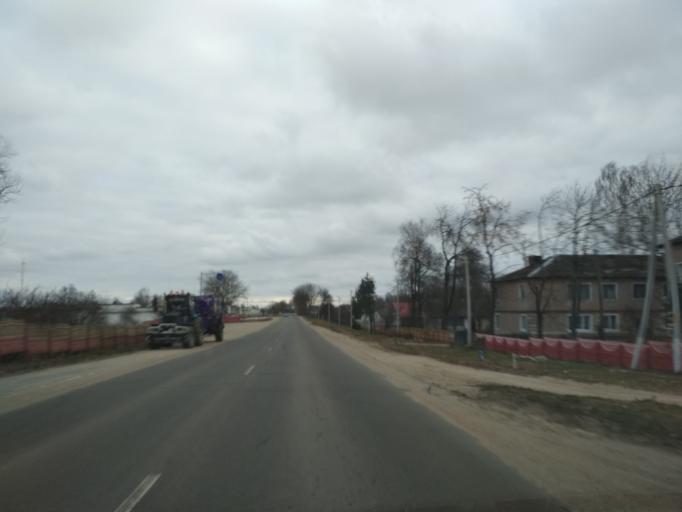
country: BY
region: Minsk
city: Svislach
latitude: 53.5708
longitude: 27.9625
